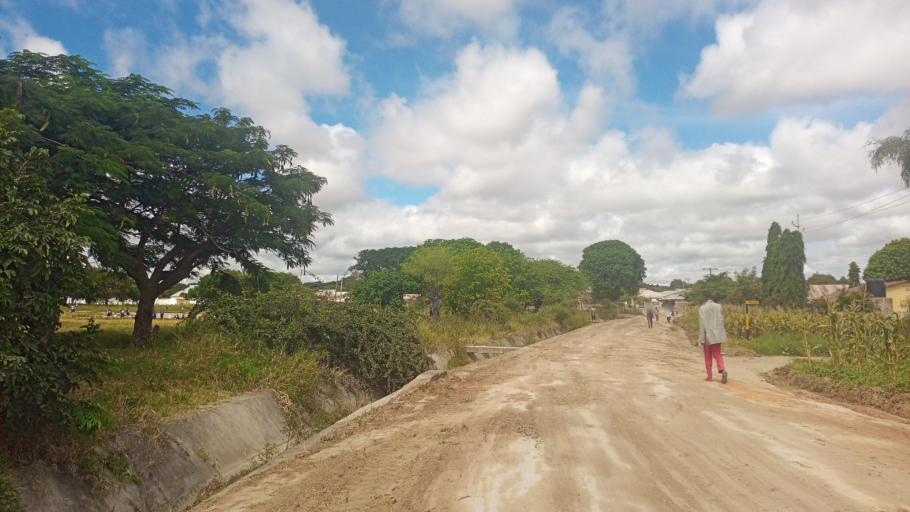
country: TZ
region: Dodoma
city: Dodoma
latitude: -6.1931
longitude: 35.7347
